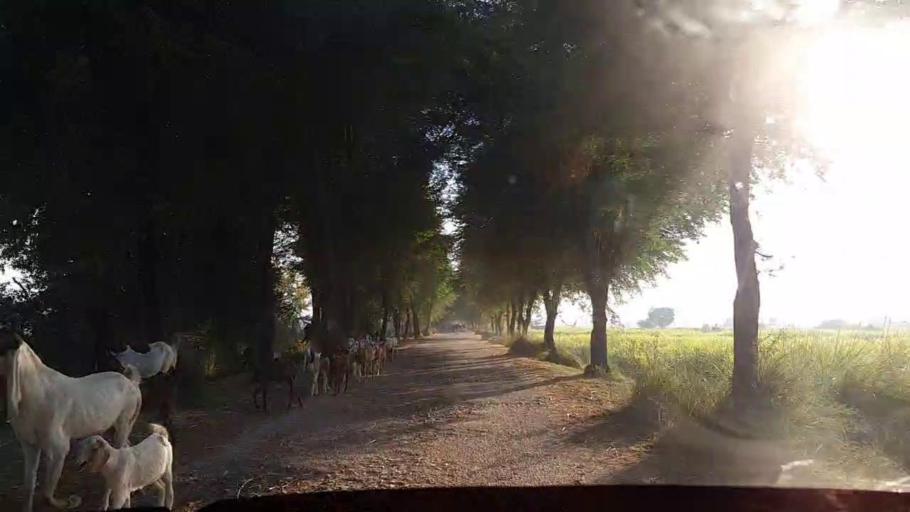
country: PK
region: Sindh
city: Sobhadero
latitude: 27.4095
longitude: 68.3938
